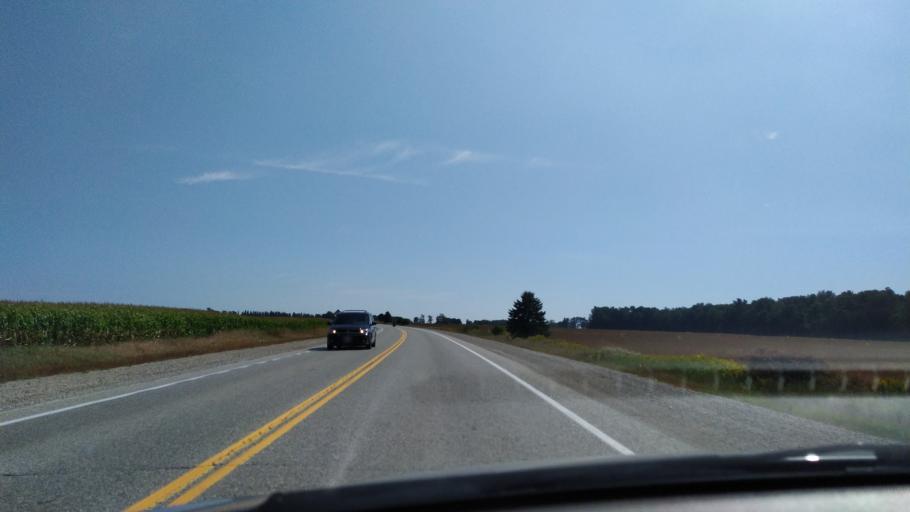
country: CA
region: Ontario
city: Ingersoll
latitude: 43.0952
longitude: -80.8714
